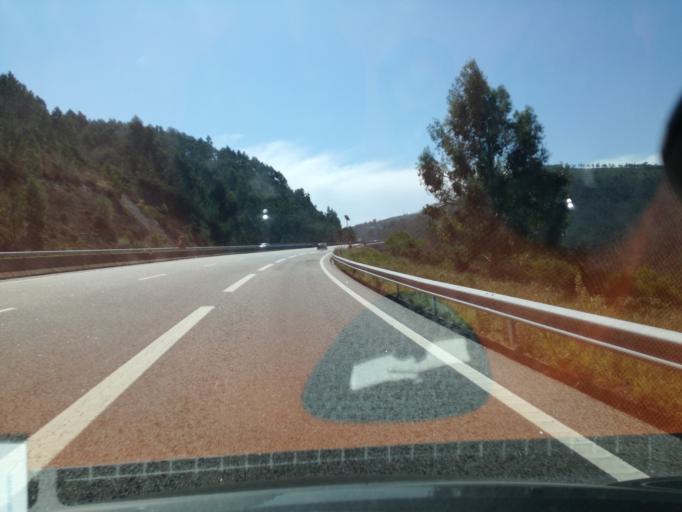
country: PT
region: Viana do Castelo
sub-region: Vila Nova de Cerveira
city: Vila Nova de Cerveira
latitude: 41.8662
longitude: -8.7808
